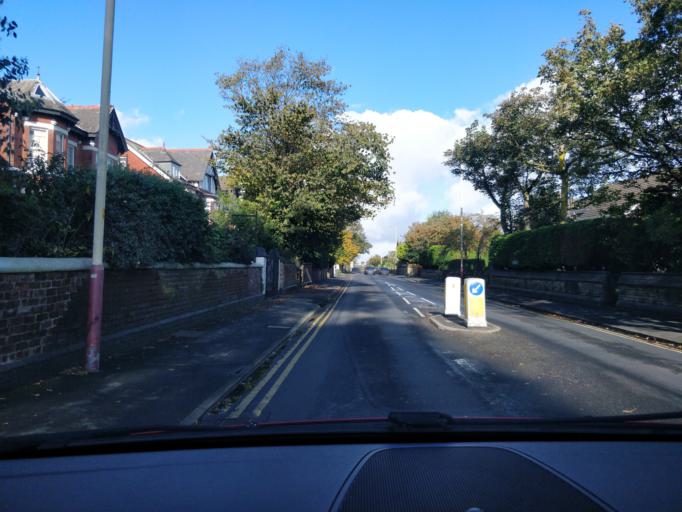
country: GB
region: England
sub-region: Sefton
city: Southport
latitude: 53.6418
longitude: -3.0096
